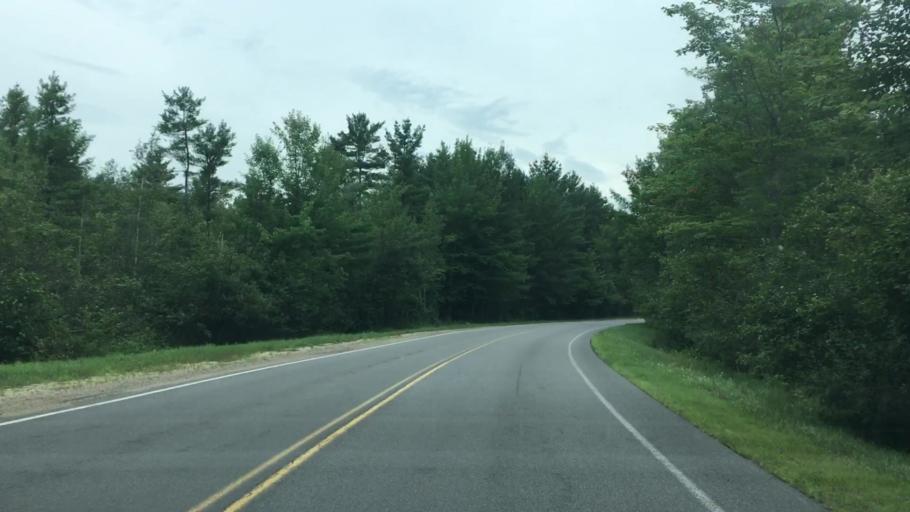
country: US
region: New York
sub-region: Essex County
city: Keeseville
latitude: 44.4776
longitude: -73.5967
